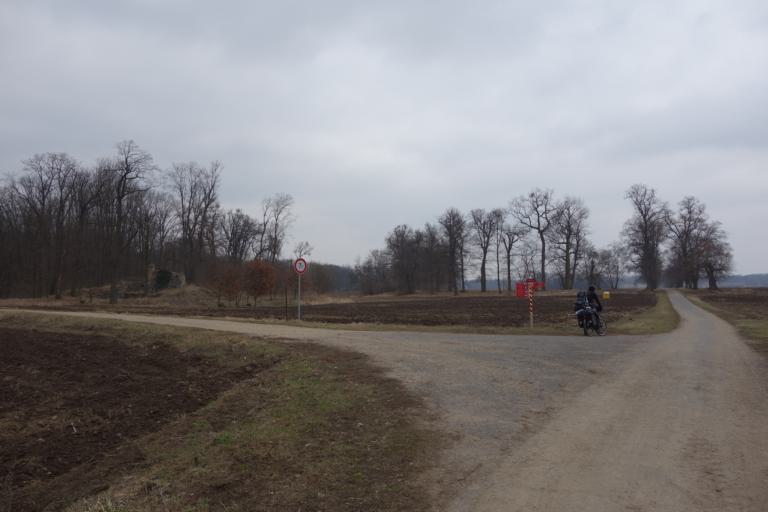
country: CZ
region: Central Bohemia
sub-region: Okres Melnik
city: Veltrusy
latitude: 50.2914
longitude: 14.3337
